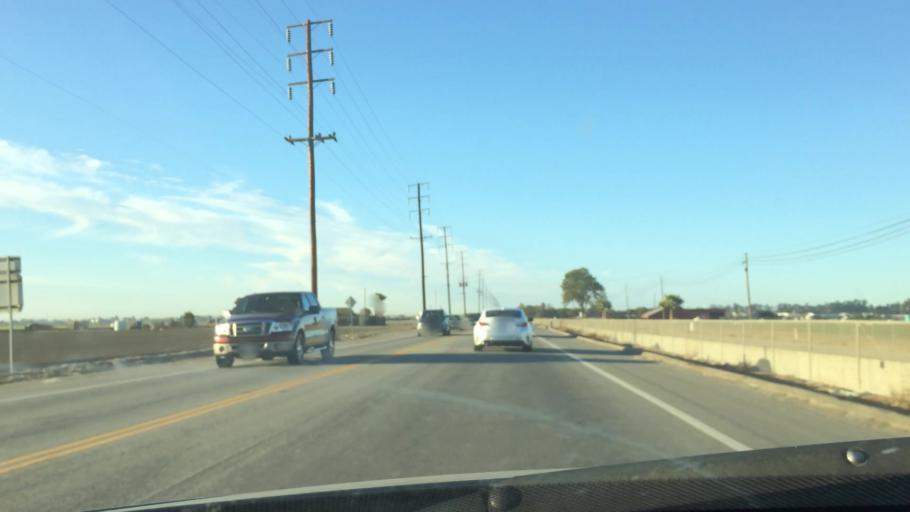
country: US
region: California
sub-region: Ventura County
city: Saticoy
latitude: 34.2512
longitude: -119.1138
